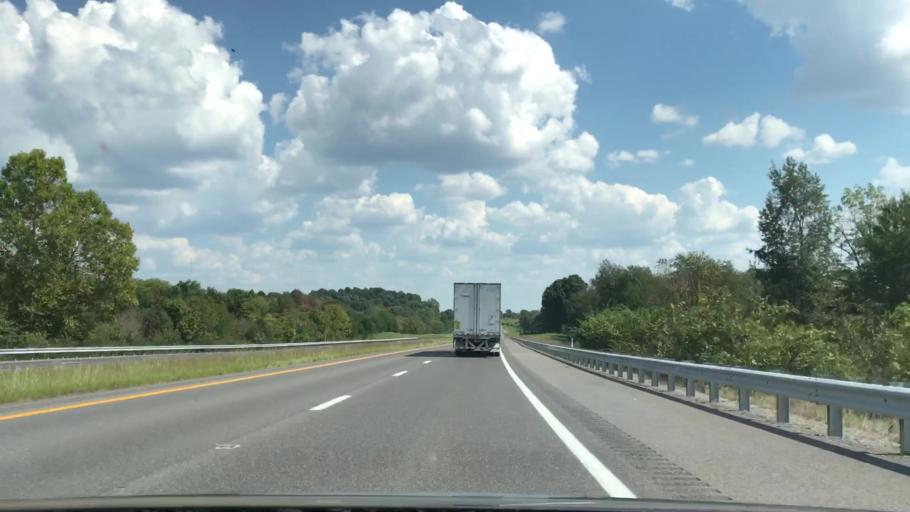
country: US
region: Kentucky
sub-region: Caldwell County
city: Princeton
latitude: 37.1106
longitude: -87.9618
